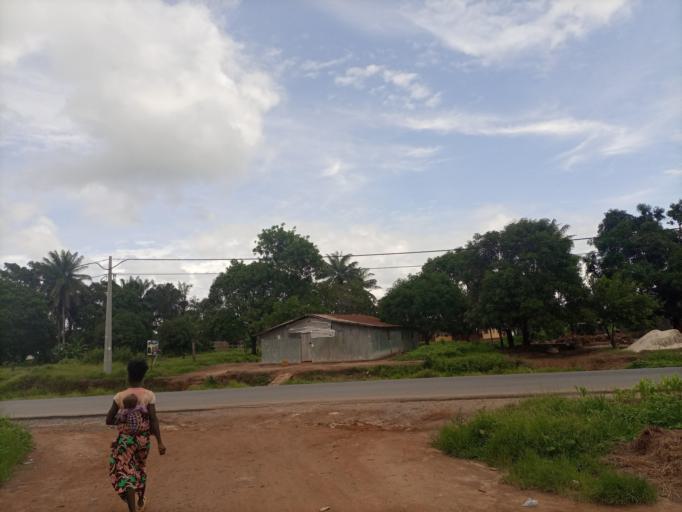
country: SL
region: Northern Province
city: Masoyila
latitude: 8.5899
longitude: -13.1656
